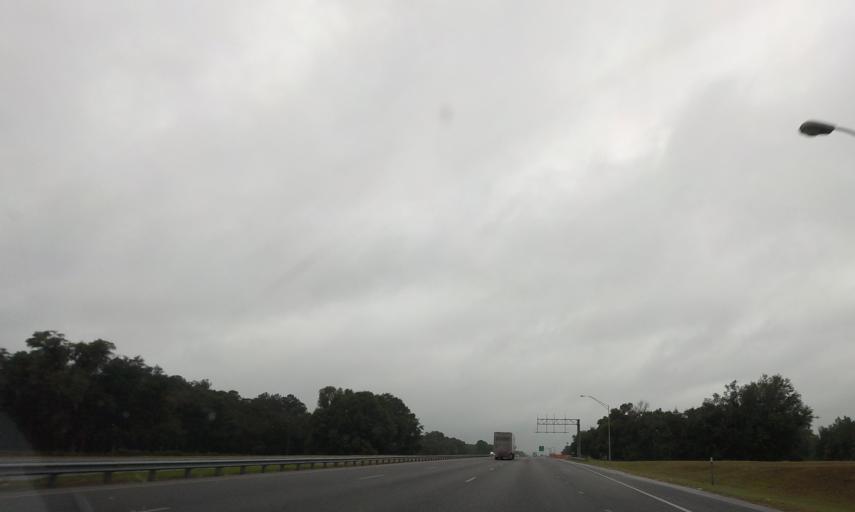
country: US
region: Georgia
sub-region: Echols County
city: Statenville
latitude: 30.6612
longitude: -83.2062
